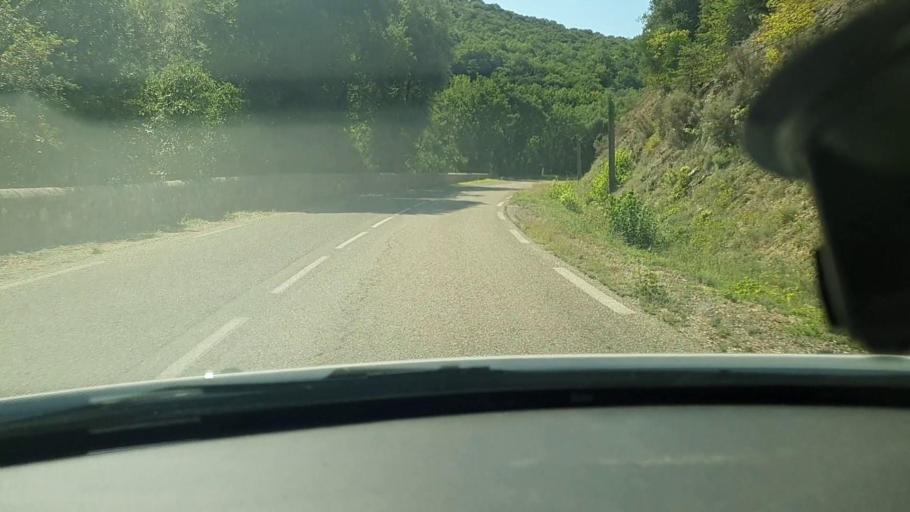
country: FR
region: Languedoc-Roussillon
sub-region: Departement du Gard
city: Saint-Paulet-de-Caisson
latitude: 44.2208
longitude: 4.5431
